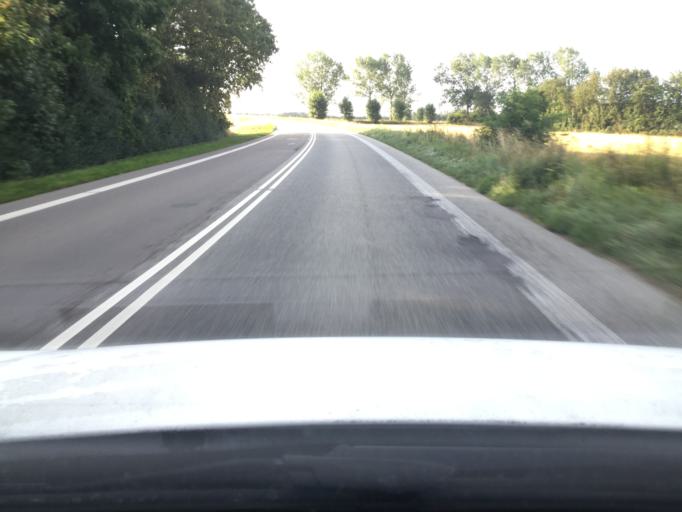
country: DK
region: Zealand
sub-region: Lolland Kommune
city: Rodby
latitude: 54.7688
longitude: 11.3005
